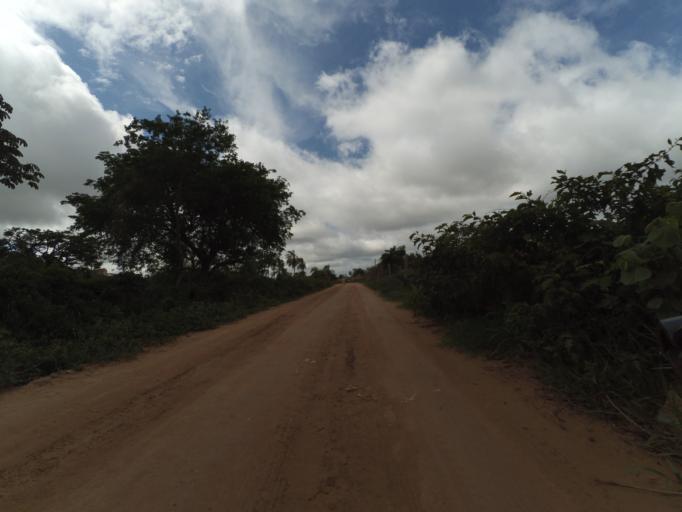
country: BO
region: Santa Cruz
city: Santa Cruz de la Sierra
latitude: -17.8778
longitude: -63.2354
